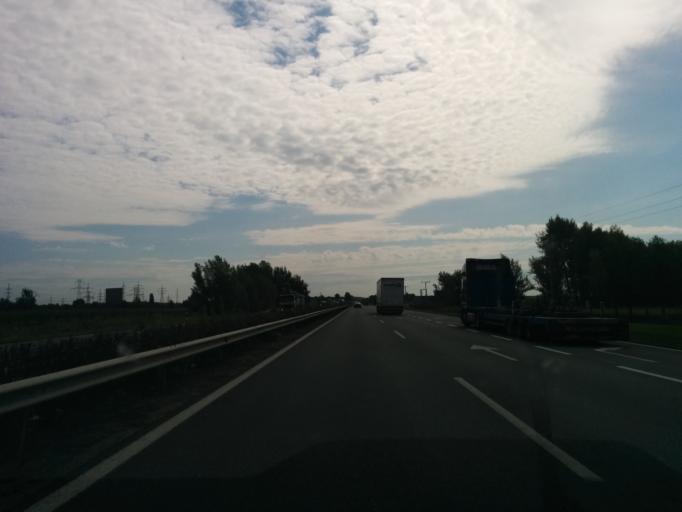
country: HU
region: Gyor-Moson-Sopron
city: Gyorujbarat
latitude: 47.6352
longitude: 17.6554
